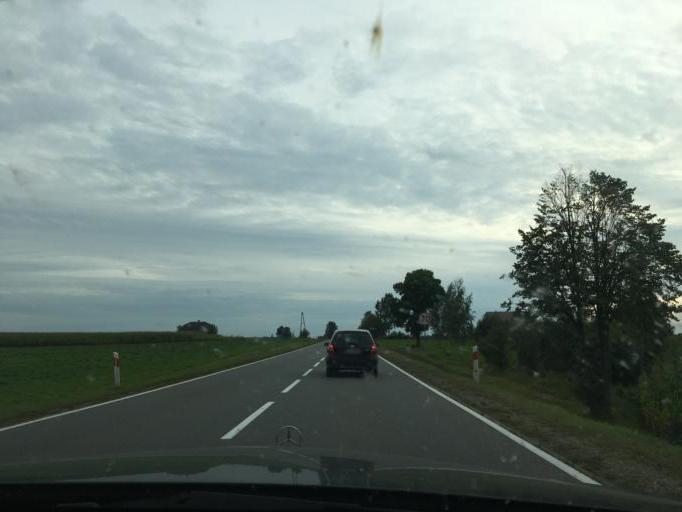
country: PL
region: Masovian Voivodeship
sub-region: Powiat ostrolecki
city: Czerwin
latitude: 52.9327
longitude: 21.8825
